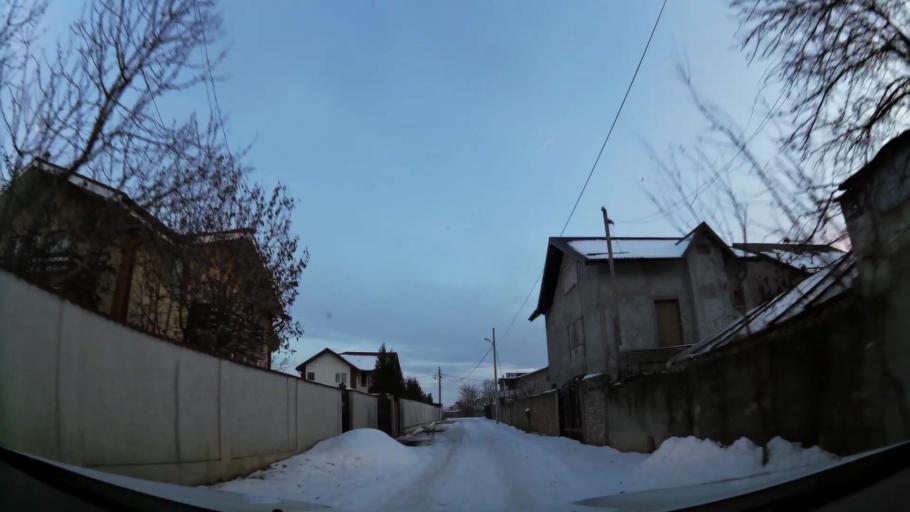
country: RO
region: Ilfov
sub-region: Comuna Magurele
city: Magurele
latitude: 44.3890
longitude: 26.0225
